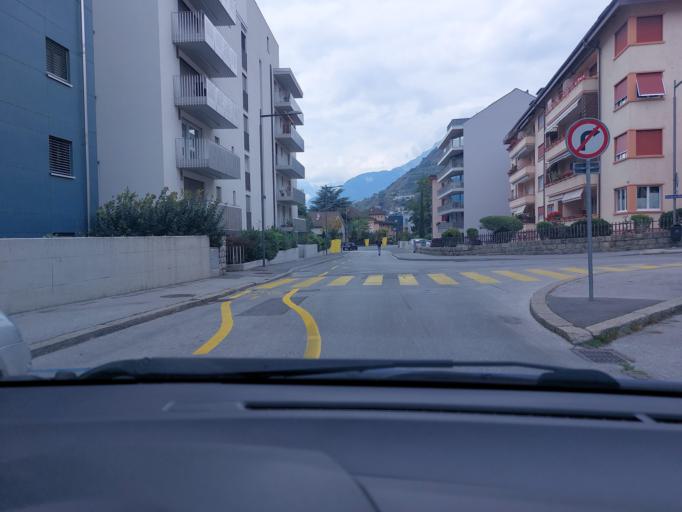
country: CH
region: Valais
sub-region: Sion District
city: Sitten
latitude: 46.2296
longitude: 7.3550
